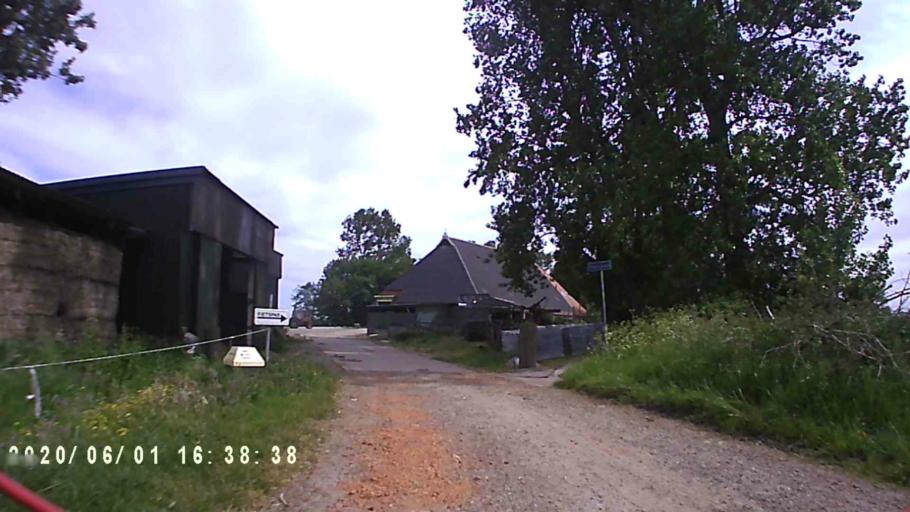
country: NL
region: Friesland
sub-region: Gemeente Leeuwarden
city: Camminghaburen
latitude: 53.1878
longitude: 5.8769
